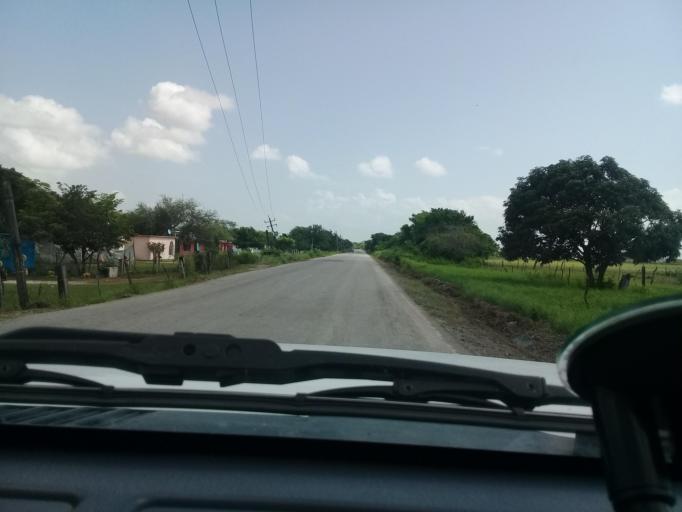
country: MX
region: Veracruz
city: Moralillo
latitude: 22.1812
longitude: -97.9471
